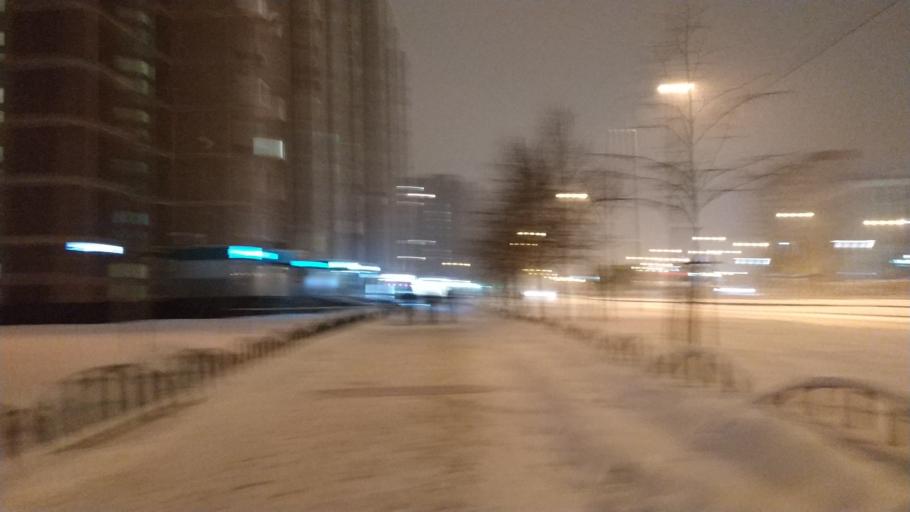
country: RU
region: Moscow
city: Zhulebino
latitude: 55.6884
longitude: 37.8595
